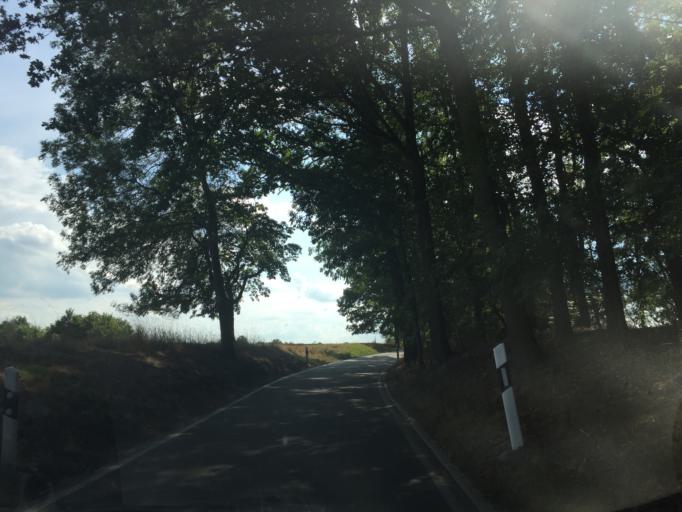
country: DE
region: Thuringia
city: Vollmershain
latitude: 50.8688
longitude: 12.3046
